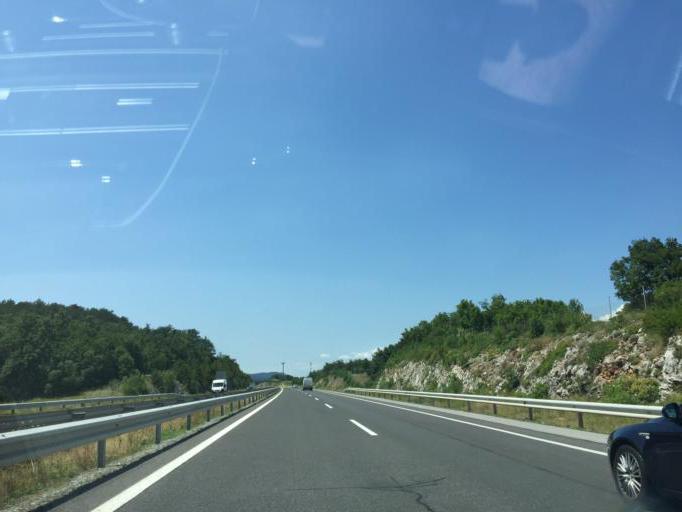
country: SI
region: Divaca
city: Divaca
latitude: 45.7083
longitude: 13.9275
